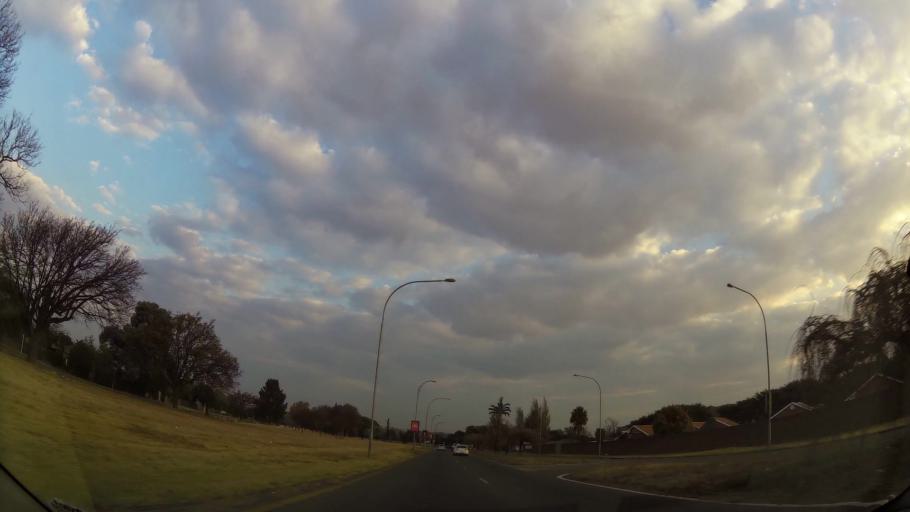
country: ZA
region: Gauteng
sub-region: Ekurhuleni Metropolitan Municipality
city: Benoni
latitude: -26.1726
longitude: 28.3108
